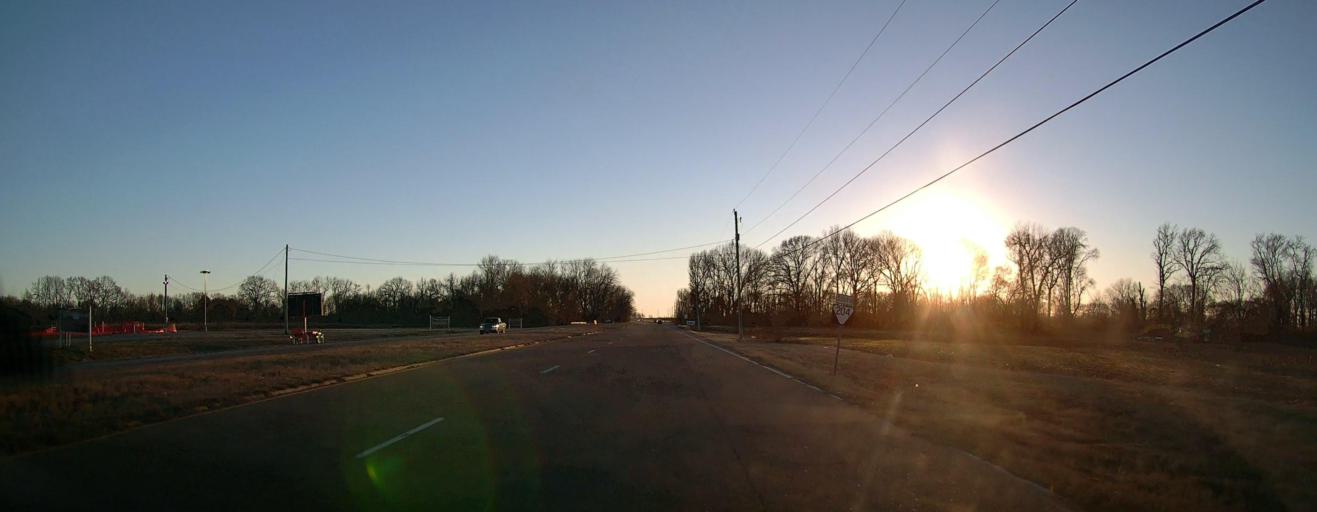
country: US
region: Tennessee
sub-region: Shelby County
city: Millington
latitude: 35.3171
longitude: -89.8755
